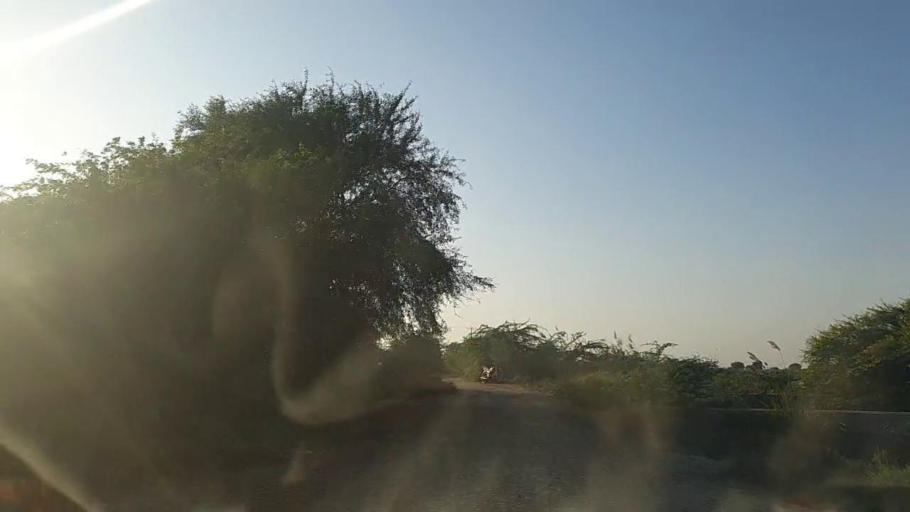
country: PK
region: Sindh
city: Jati
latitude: 24.4168
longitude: 68.1827
